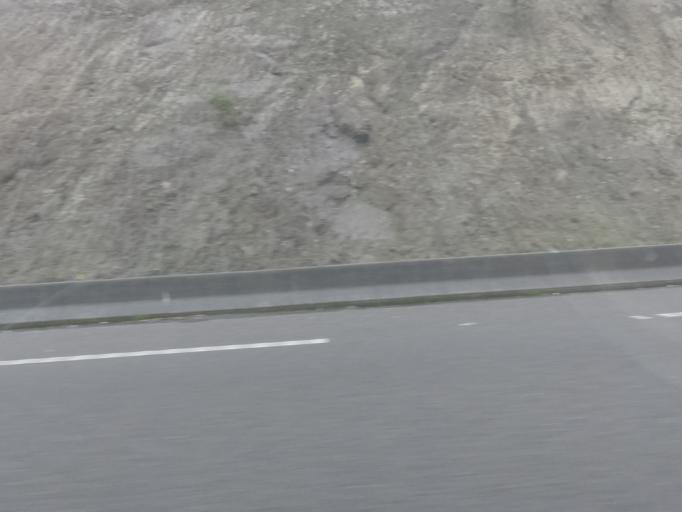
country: ES
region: Galicia
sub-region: Provincia da Coruna
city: Santiago de Compostela
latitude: 42.8508
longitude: -8.5320
